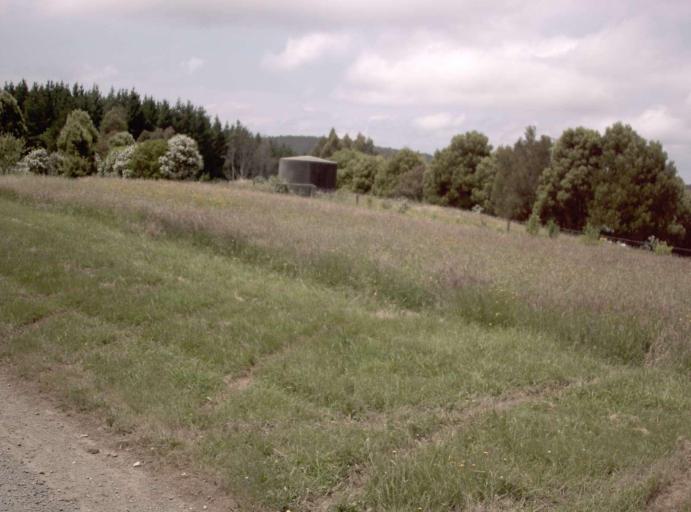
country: AU
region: Victoria
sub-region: Latrobe
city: Traralgon
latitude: -38.3901
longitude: 146.6604
